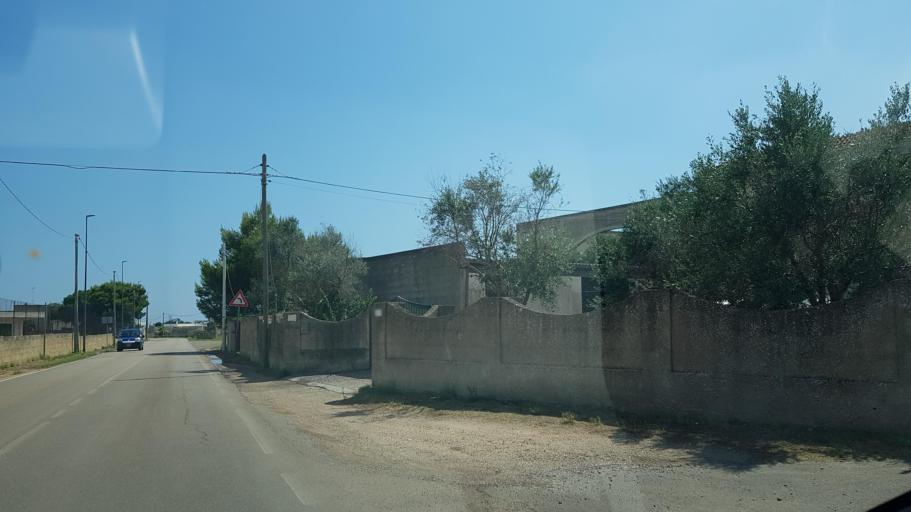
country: IT
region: Apulia
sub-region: Provincia di Lecce
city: Castrignano del Capo
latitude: 39.8270
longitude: 18.3523
